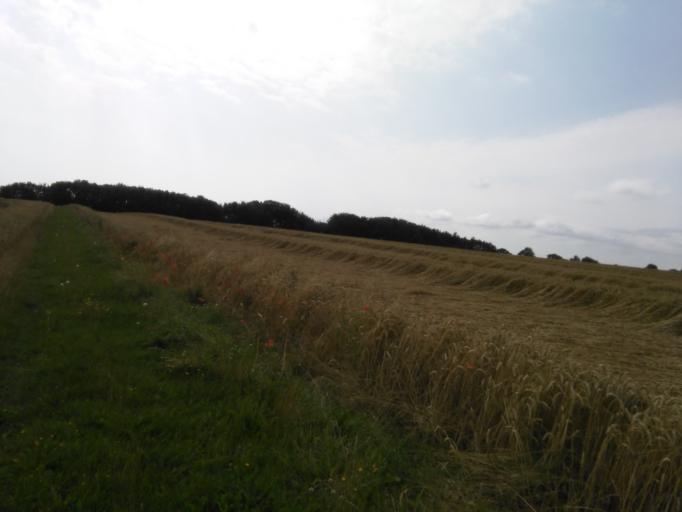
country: DK
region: Central Jutland
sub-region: Odder Kommune
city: Odder
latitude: 55.8788
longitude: 10.0375
